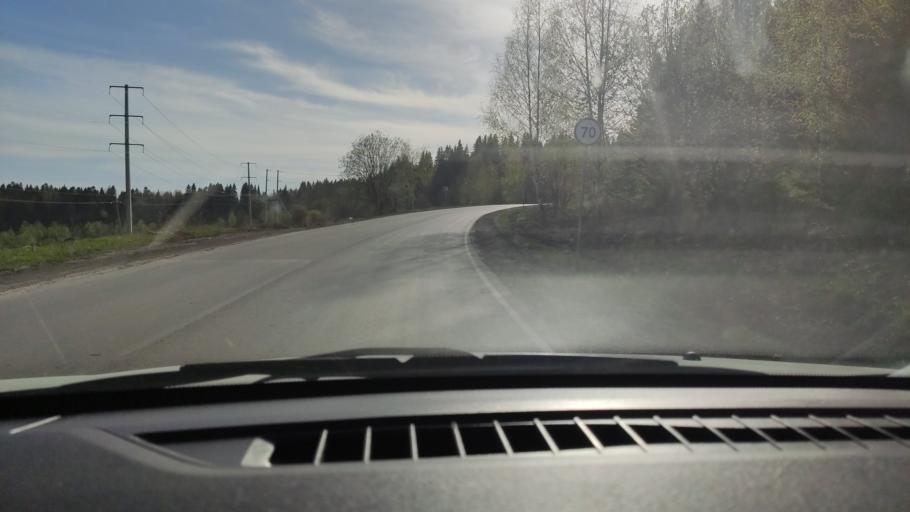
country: RU
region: Perm
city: Novyye Lyady
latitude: 57.9206
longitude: 56.6619
